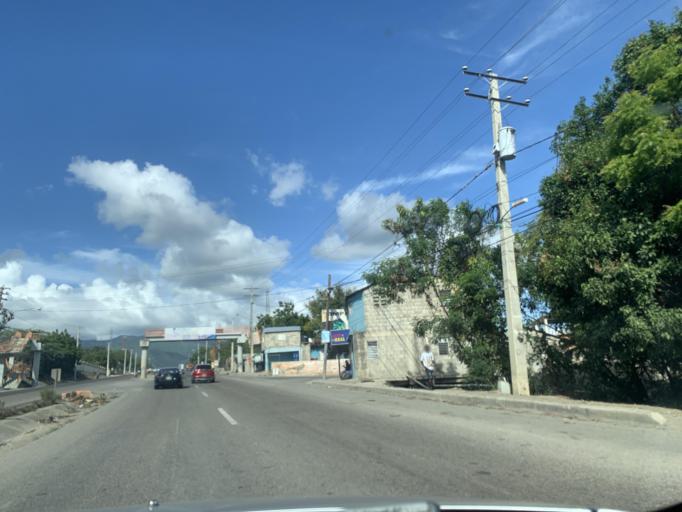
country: DO
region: Santiago
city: Villa Bisono
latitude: 19.5494
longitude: -70.8336
